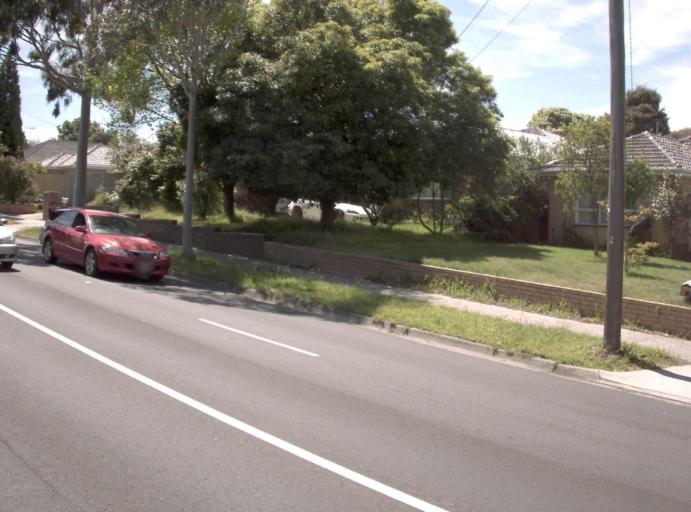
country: AU
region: Victoria
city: Burwood East
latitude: -37.8669
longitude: 145.1493
